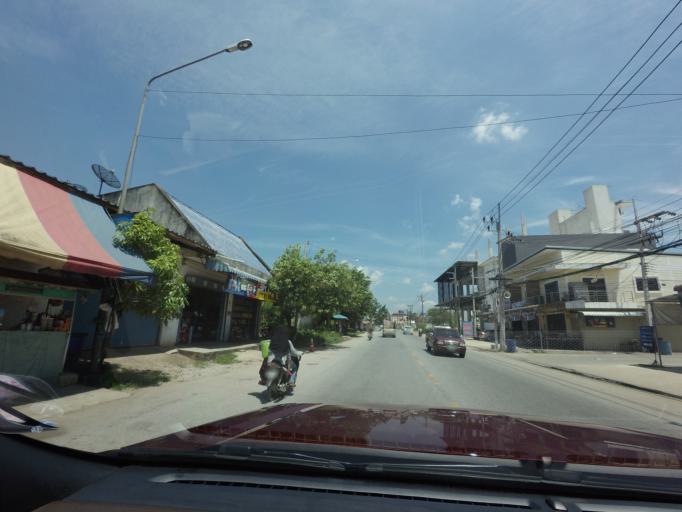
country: TH
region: Yala
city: Yala
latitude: 6.5557
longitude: 101.2726
